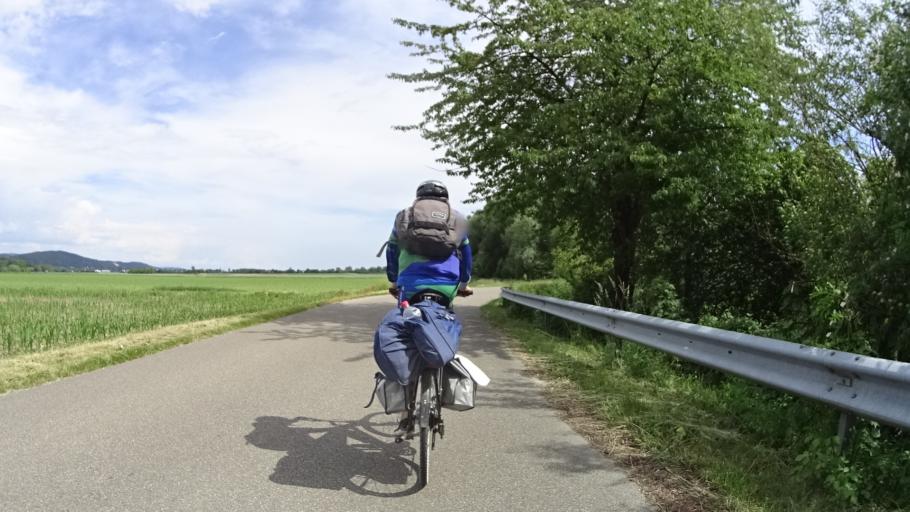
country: DE
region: Bavaria
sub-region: Upper Palatinate
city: Wiesent
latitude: 49.0056
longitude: 12.3388
